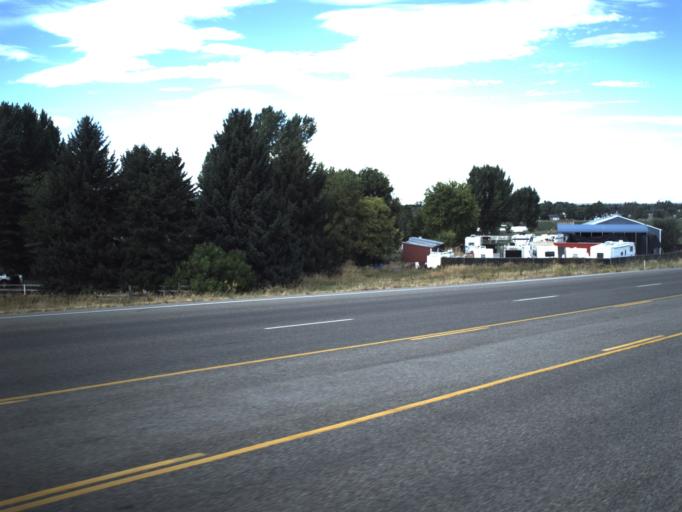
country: US
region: Utah
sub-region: Cache County
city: Wellsville
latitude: 41.6210
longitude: -111.9292
